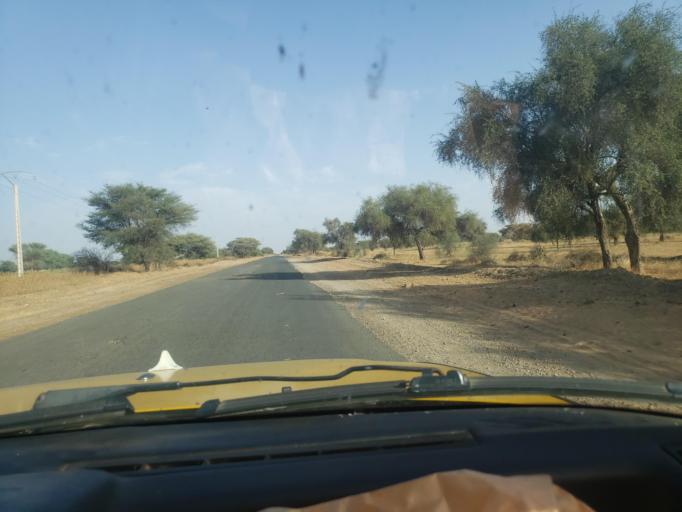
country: SN
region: Louga
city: Louga
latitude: 15.5047
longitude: -15.9559
